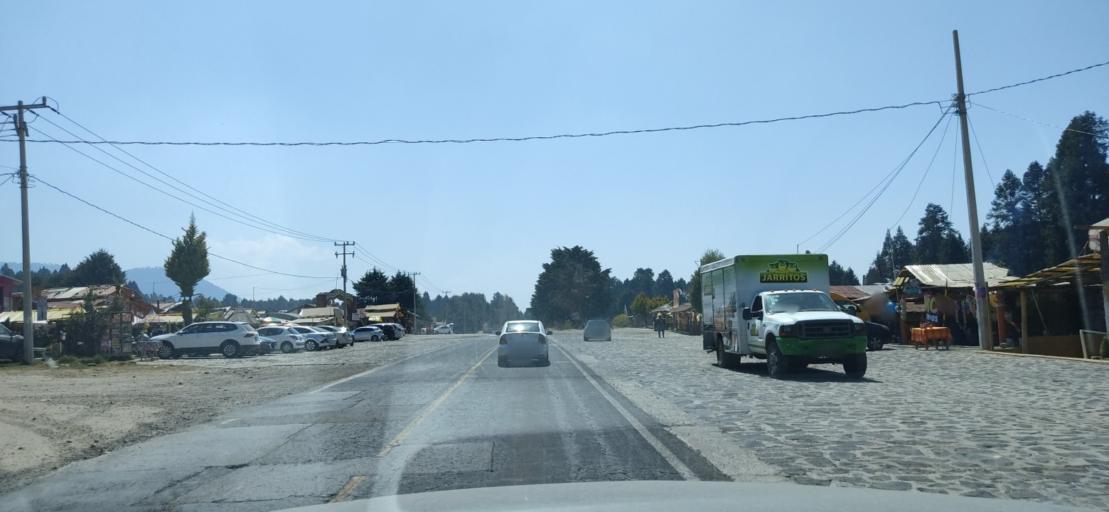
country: MX
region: Mexico
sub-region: Ocoyoacac
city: San Jeronimo Acazulco
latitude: 19.2703
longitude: -99.3761
